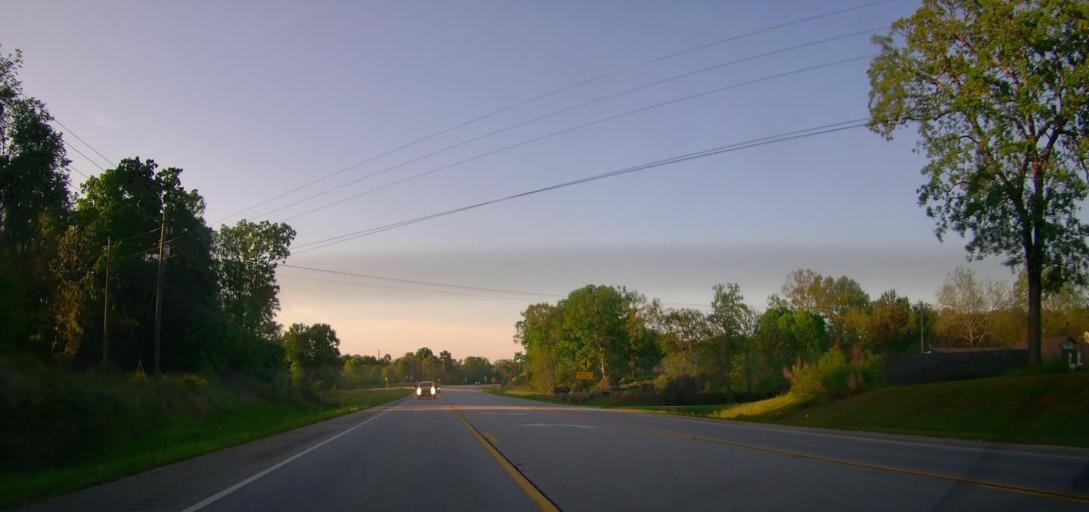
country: US
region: Georgia
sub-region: Newton County
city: Oakwood
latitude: 33.5342
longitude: -83.9523
